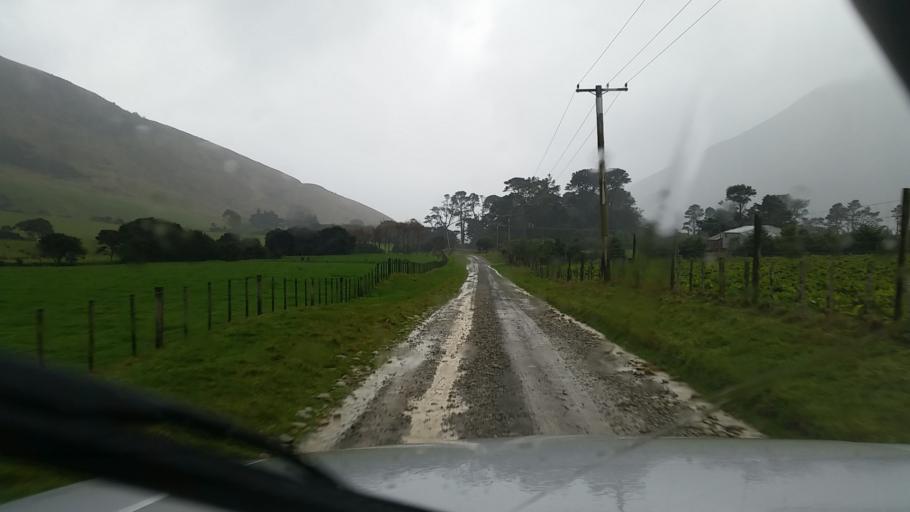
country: NZ
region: Marlborough
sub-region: Marlborough District
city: Picton
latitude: -41.1180
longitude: 174.0368
